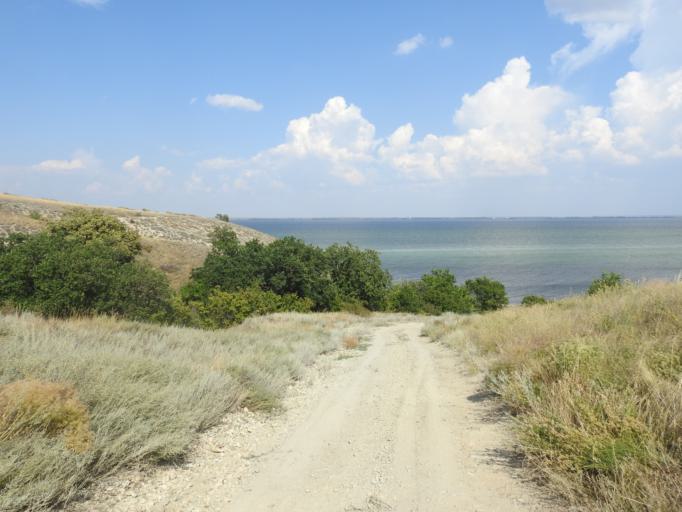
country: RU
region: Saratov
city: Rovnoye
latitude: 50.4922
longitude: 45.7991
